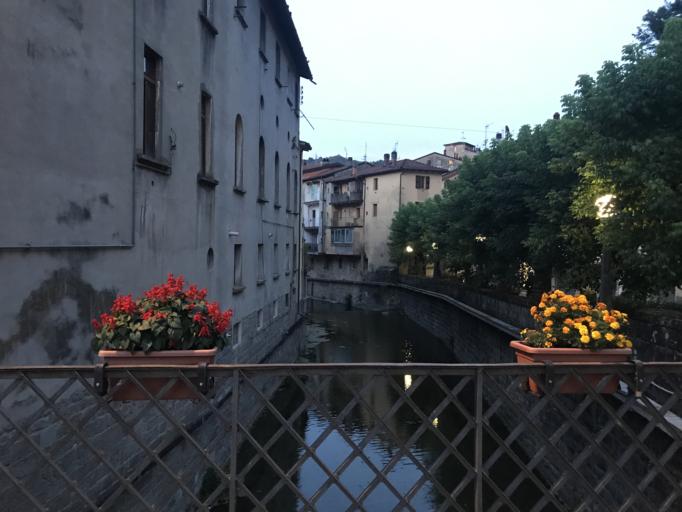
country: IT
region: Emilia-Romagna
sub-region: Provincia di Bologna
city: Berzantina
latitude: 44.1539
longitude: 10.9749
